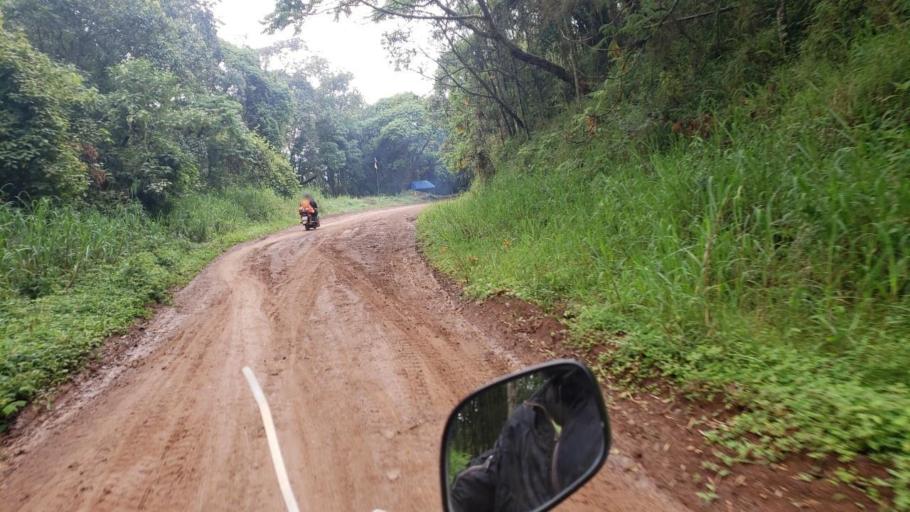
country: CD
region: South Kivu
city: Kabare
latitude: -2.2623
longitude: 28.6566
